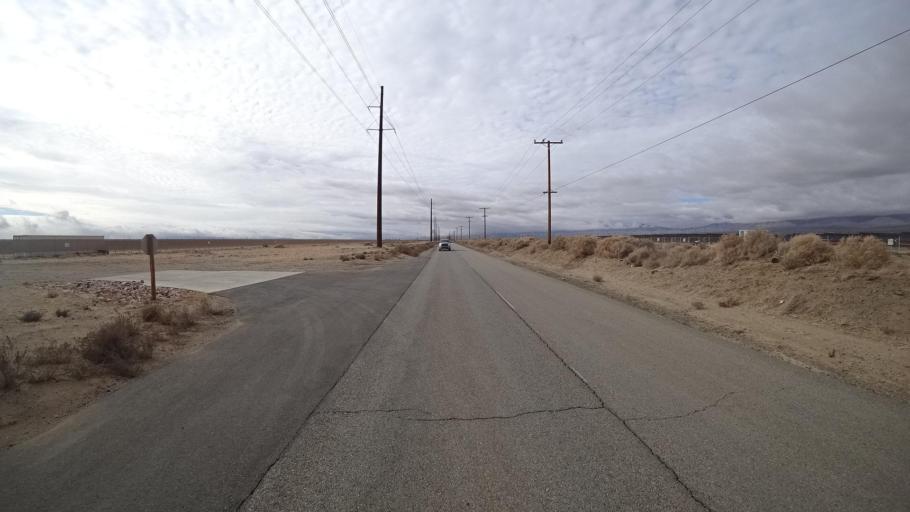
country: US
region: California
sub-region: Kern County
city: Rosamond
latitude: 34.8633
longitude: -118.3309
